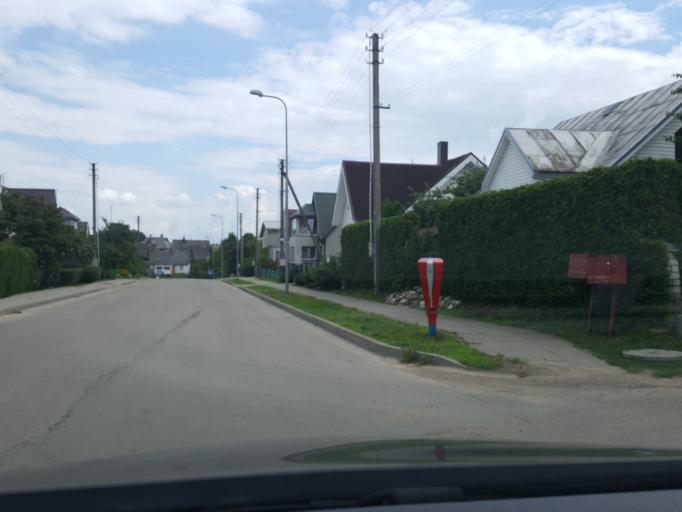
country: LT
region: Alytaus apskritis
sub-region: Alytus
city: Alytus
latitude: 54.4026
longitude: 24.0453
